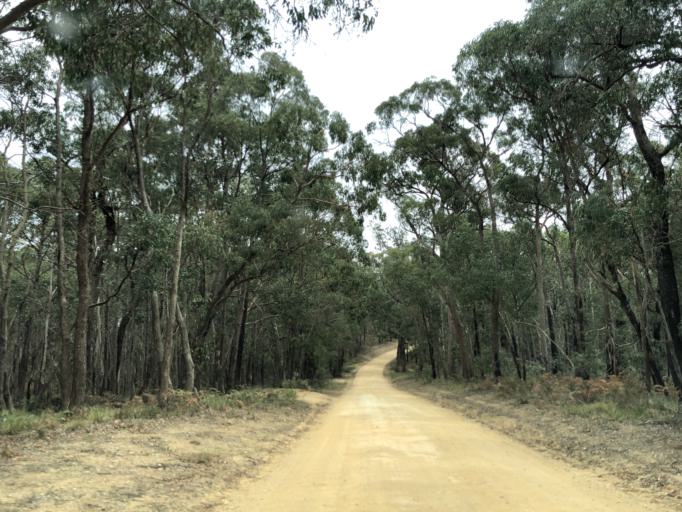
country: AU
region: Victoria
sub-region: Moorabool
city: Bacchus Marsh
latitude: -37.5009
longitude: 144.3438
